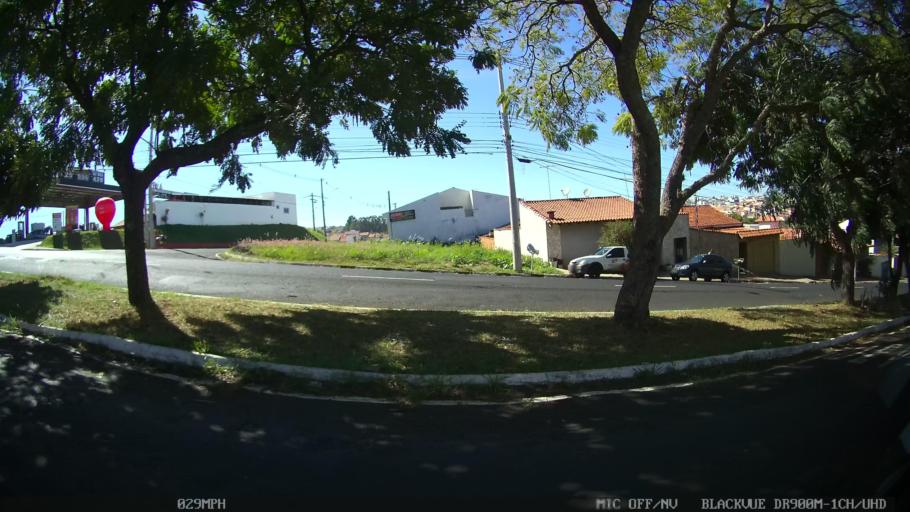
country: BR
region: Sao Paulo
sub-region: Franca
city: Franca
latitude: -20.5491
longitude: -47.3730
